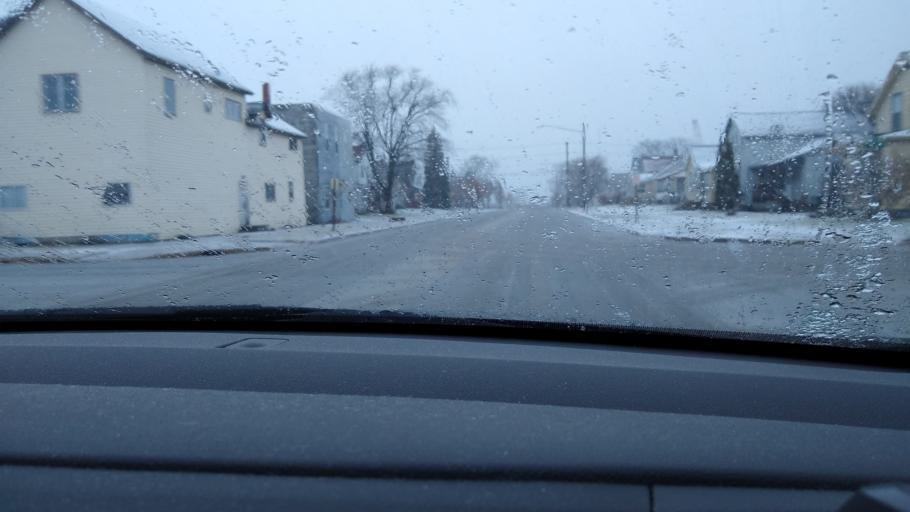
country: US
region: Michigan
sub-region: Delta County
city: Escanaba
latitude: 45.7467
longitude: -87.0612
